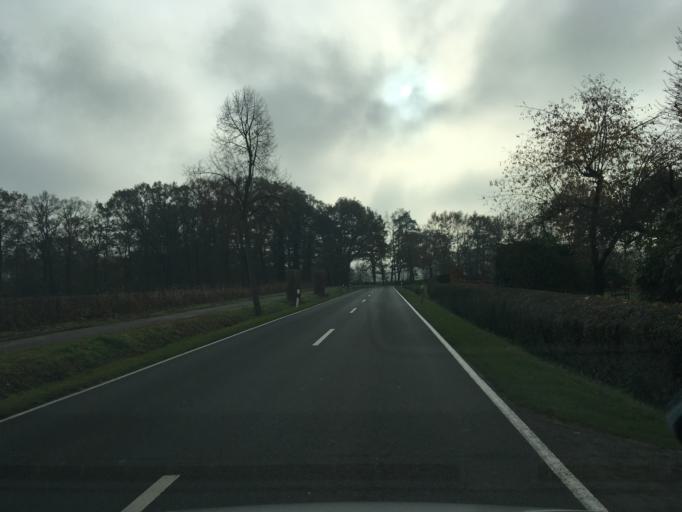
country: DE
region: North Rhine-Westphalia
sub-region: Regierungsbezirk Munster
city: Sudlohn
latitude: 51.9040
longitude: 6.9181
